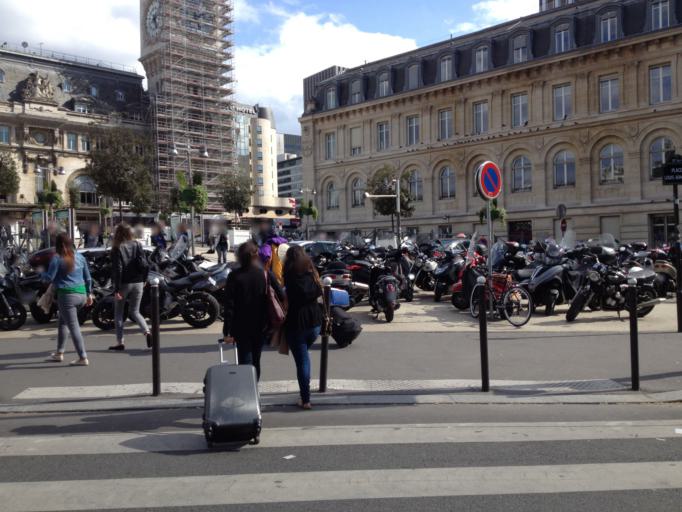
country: FR
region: Ile-de-France
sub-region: Paris
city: Paris
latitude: 48.8457
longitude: 2.3725
